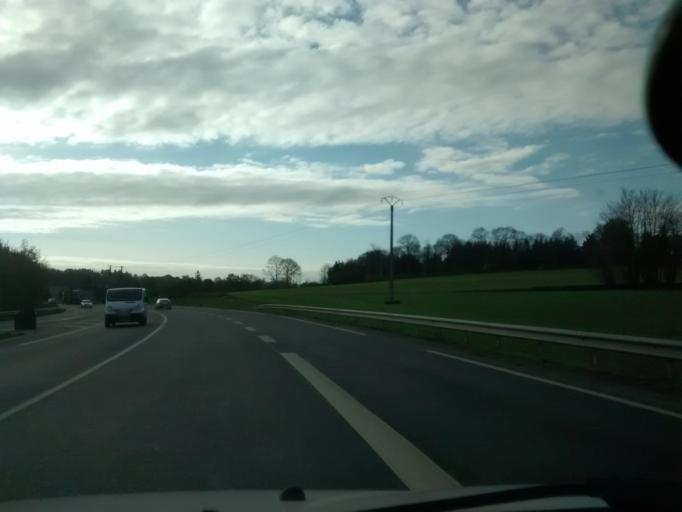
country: FR
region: Brittany
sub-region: Departement d'Ille-et-Vilaine
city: Poce-les-Bois
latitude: 48.1219
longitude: -1.2333
